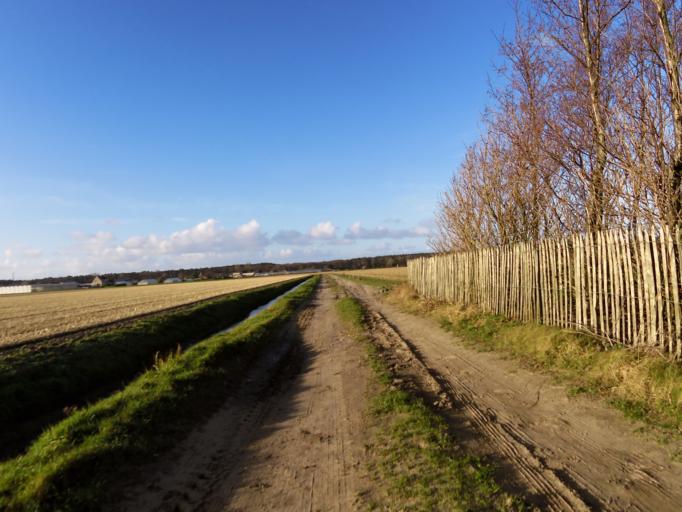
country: NL
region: South Holland
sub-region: Gemeente Noordwijkerhout
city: Noordwijkerhout
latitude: 52.2696
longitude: 4.4872
